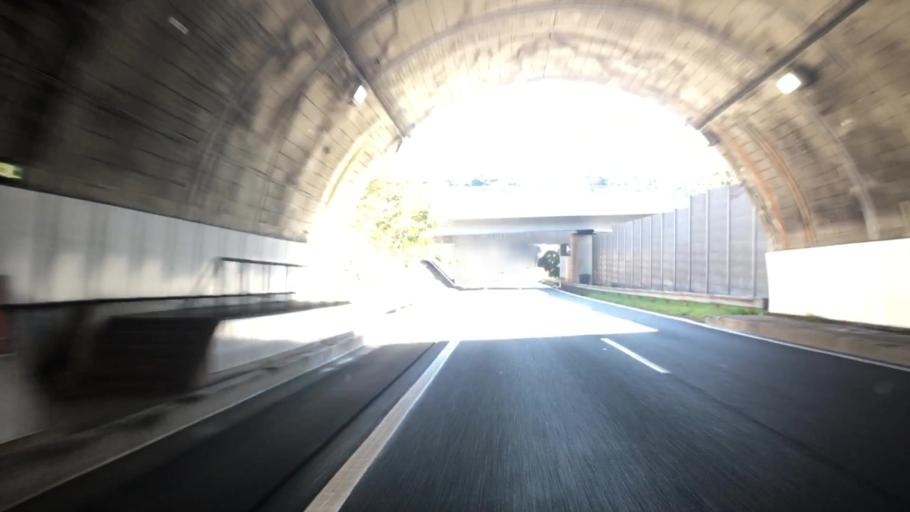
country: JP
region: Kanagawa
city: Zushi
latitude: 35.3258
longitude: 139.5982
